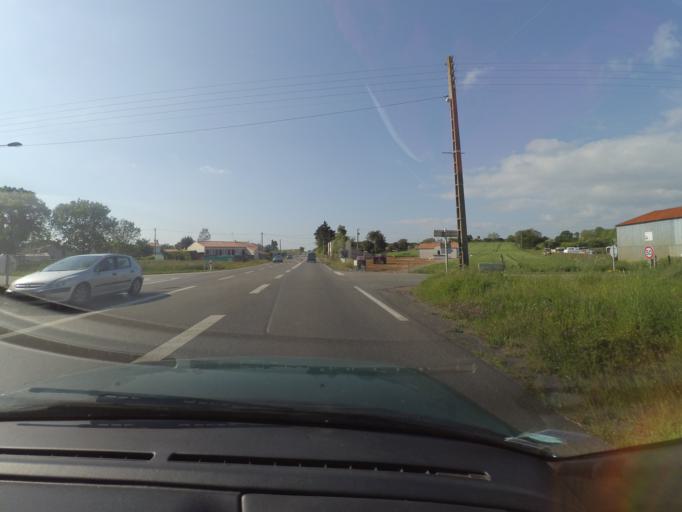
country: FR
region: Pays de la Loire
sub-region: Departement de la Vendee
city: Angles
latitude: 46.4255
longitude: -1.3952
